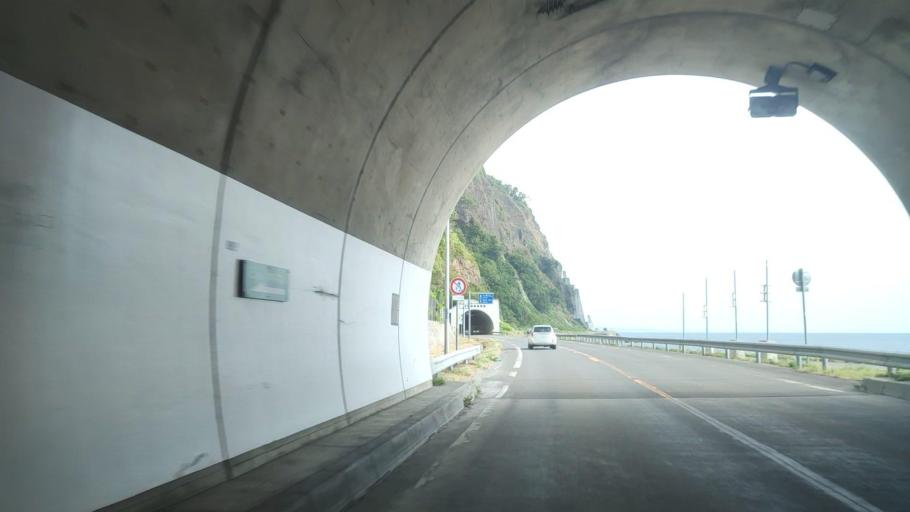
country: JP
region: Hokkaido
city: Ishikari
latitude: 43.4707
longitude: 141.3962
